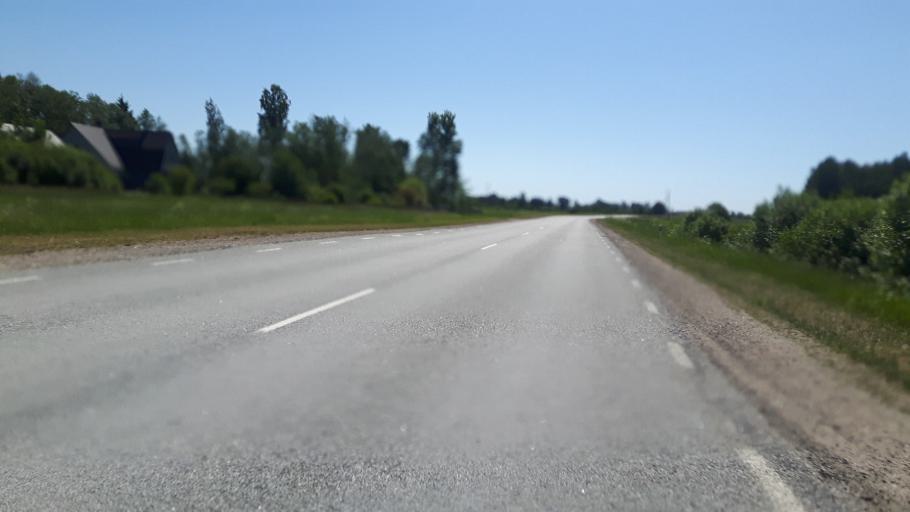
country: EE
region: Paernumaa
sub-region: Sindi linn
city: Sindi
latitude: 58.4549
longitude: 24.7780
